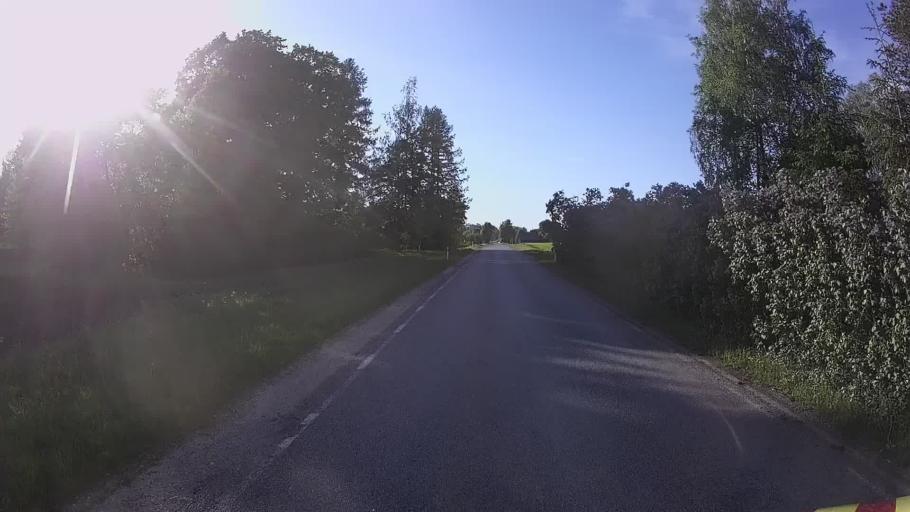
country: EE
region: Laeaene-Virumaa
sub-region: Vinni vald
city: Vinni
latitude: 59.3000
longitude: 26.5734
